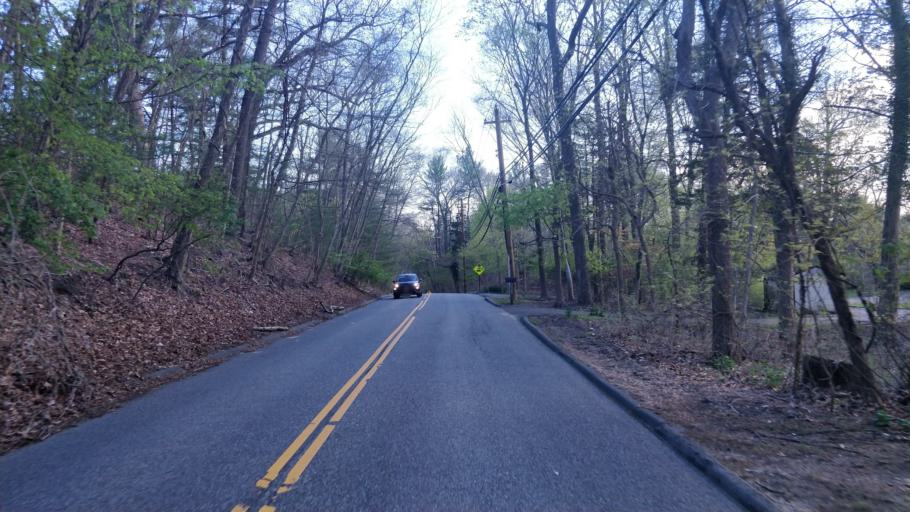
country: US
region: New York
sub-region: Suffolk County
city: Village of the Branch
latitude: 40.8742
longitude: -73.1896
